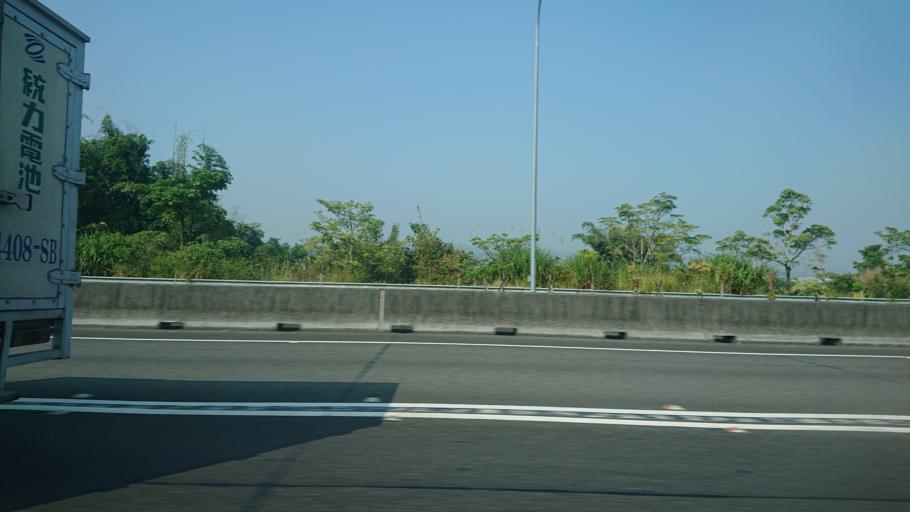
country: TW
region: Taiwan
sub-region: Nantou
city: Nantou
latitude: 23.8736
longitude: 120.7063
